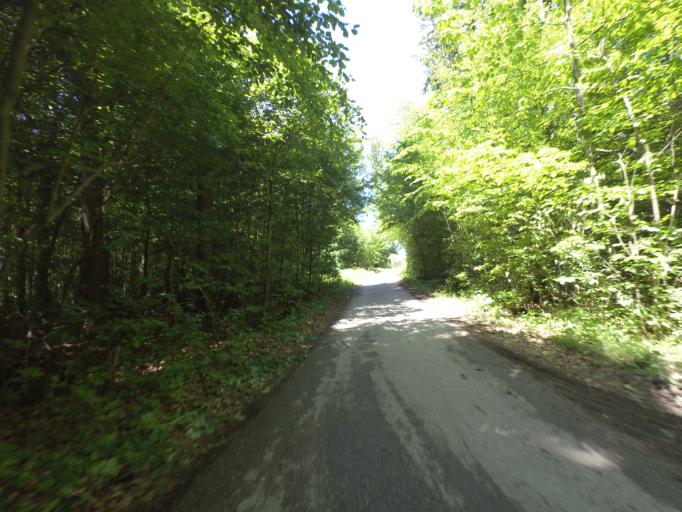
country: DE
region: Bavaria
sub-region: Upper Bavaria
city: Waging am See
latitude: 47.9453
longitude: 12.7372
